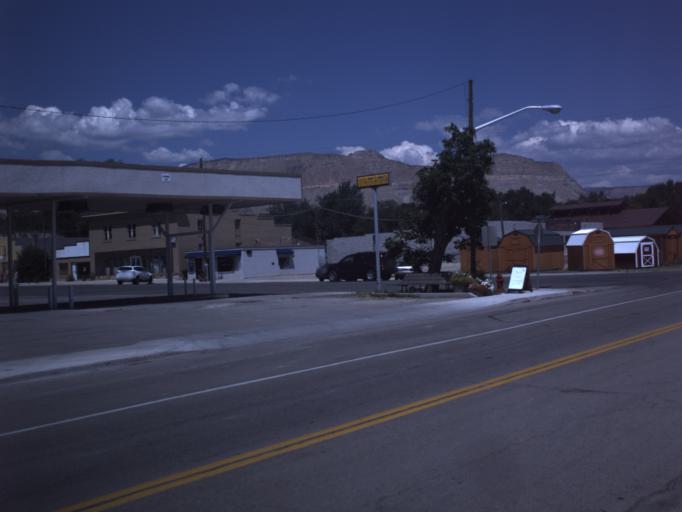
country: US
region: Utah
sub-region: Emery County
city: Ferron
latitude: 39.0896
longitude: -111.1320
